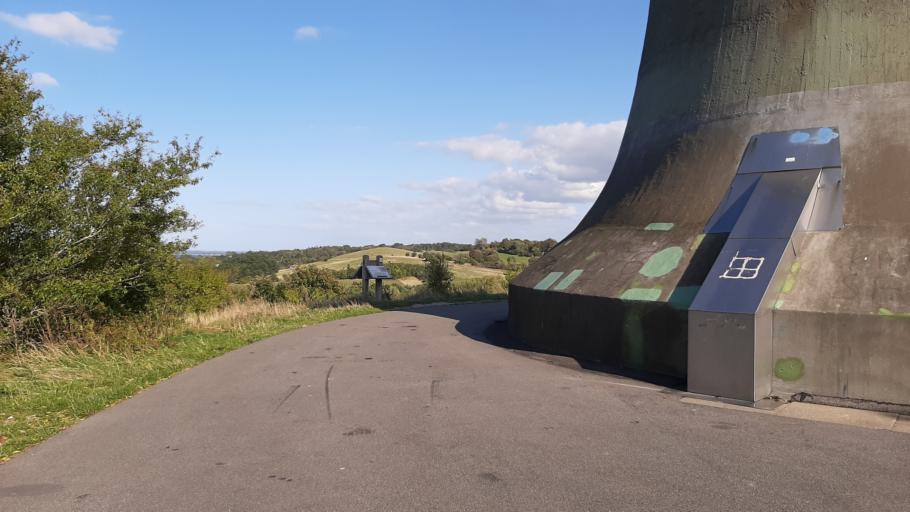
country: DK
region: Zealand
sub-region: Odsherred Kommune
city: Asnaes
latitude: 55.8296
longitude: 11.4217
